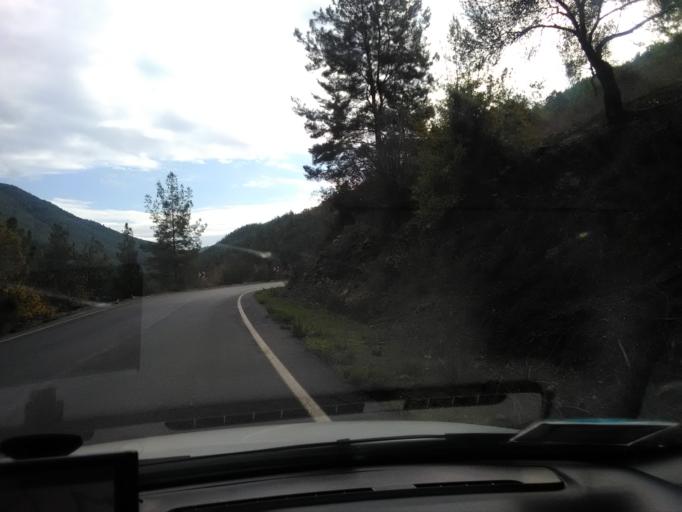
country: TR
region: Antalya
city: Gazipasa
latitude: 36.2499
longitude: 32.4064
